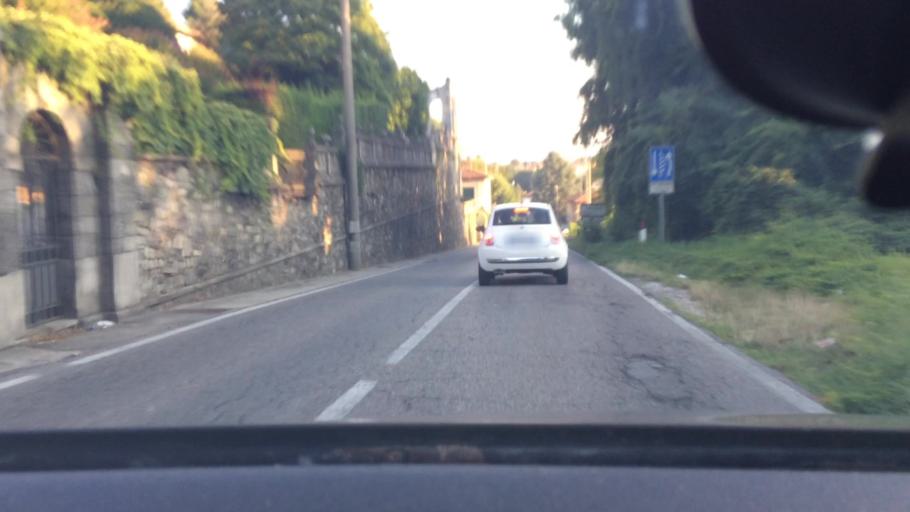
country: IT
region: Lombardy
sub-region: Provincia di Como
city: Cadorago-Caslino al Piano
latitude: 45.7334
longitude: 9.0418
